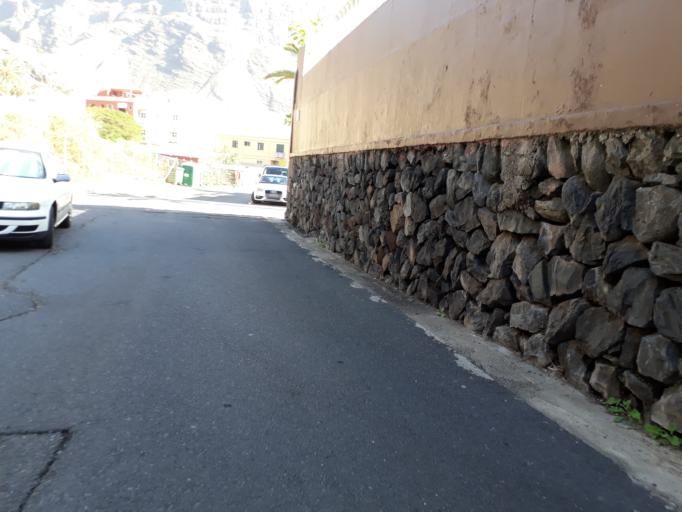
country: ES
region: Canary Islands
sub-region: Provincia de Santa Cruz de Tenerife
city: Alajero
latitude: 28.0965
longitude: -17.3444
